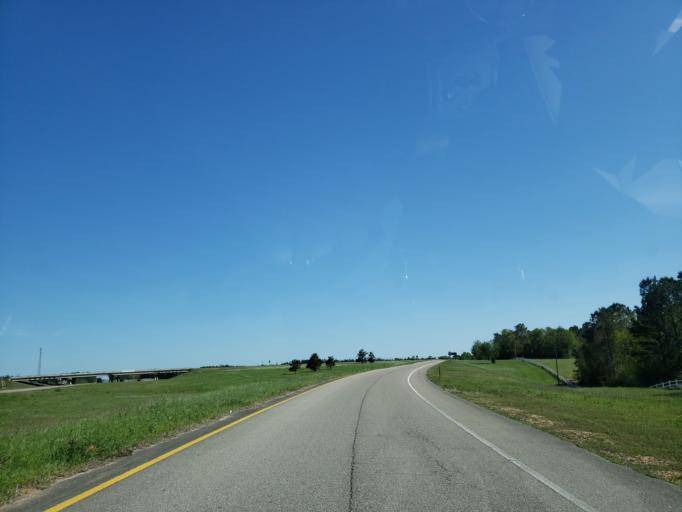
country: US
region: Mississippi
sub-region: Harrison County
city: Lyman
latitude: 30.5558
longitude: -89.0297
